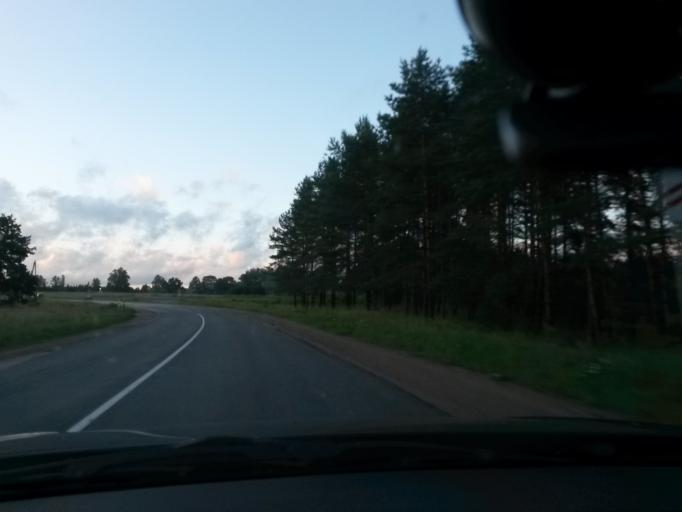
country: LV
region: Jekabpils Rajons
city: Jekabpils
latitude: 56.6882
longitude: 25.9866
